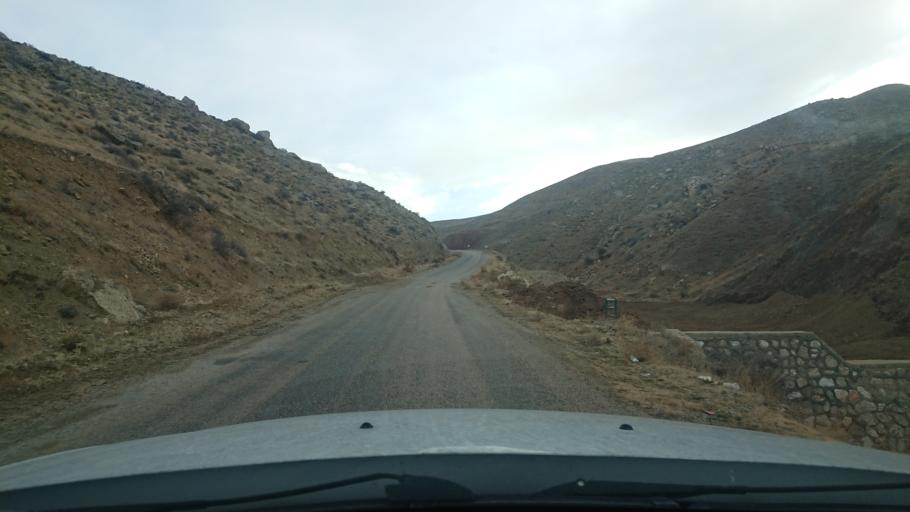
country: TR
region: Aksaray
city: Acipinar
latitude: 38.6218
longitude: 33.7906
